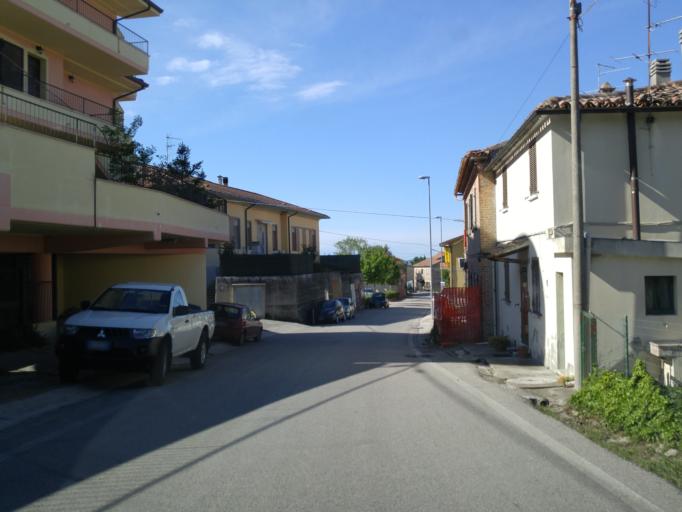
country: IT
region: The Marches
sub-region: Provincia di Pesaro e Urbino
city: Mombaroccio
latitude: 43.8152
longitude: 12.8490
